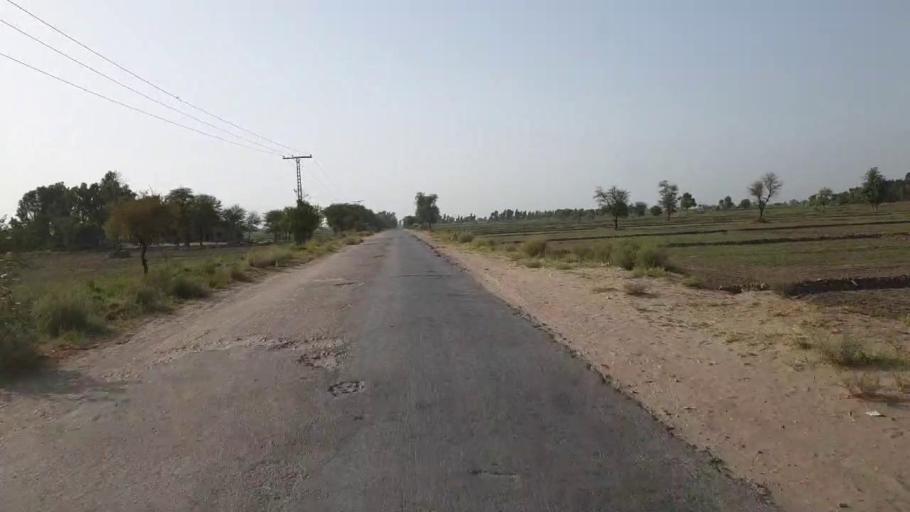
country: PK
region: Sindh
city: Jam Sahib
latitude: 26.3854
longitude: 68.8836
